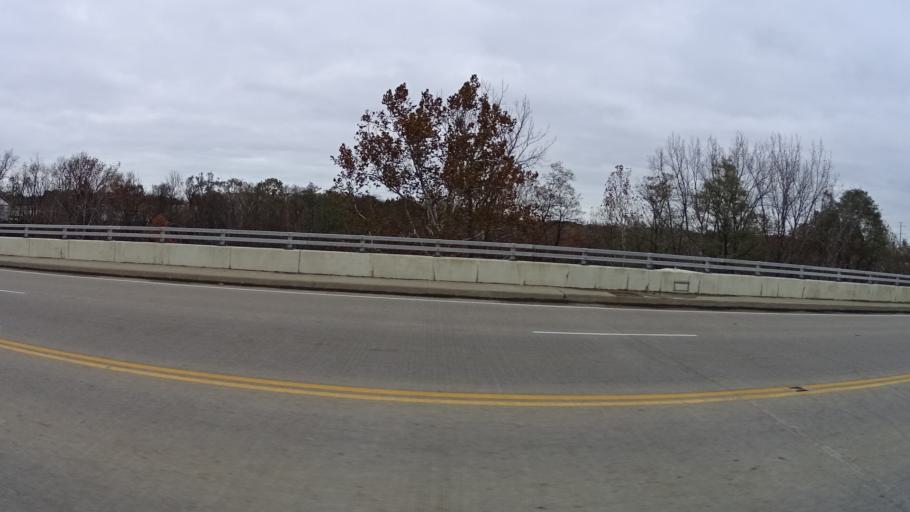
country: US
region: Ohio
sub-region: Lorain County
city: Sheffield
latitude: 41.4206
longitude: -82.1001
